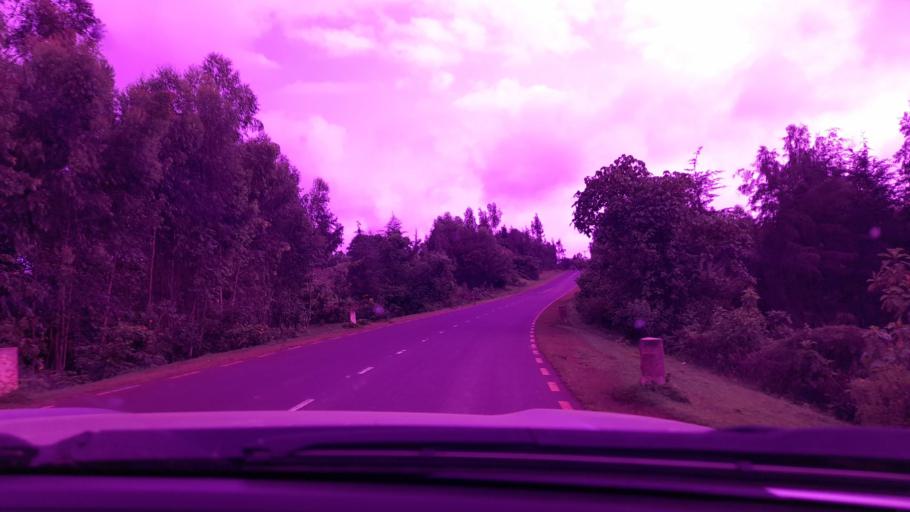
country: ET
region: Oromiya
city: Bedele
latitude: 8.2961
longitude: 36.4492
